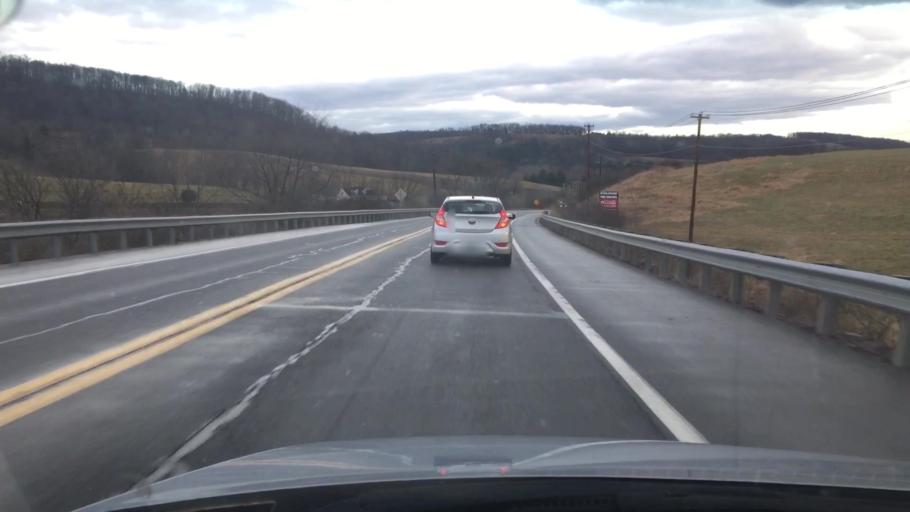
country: US
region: Pennsylvania
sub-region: Columbia County
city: Bloomsburg
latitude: 41.0209
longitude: -76.4884
